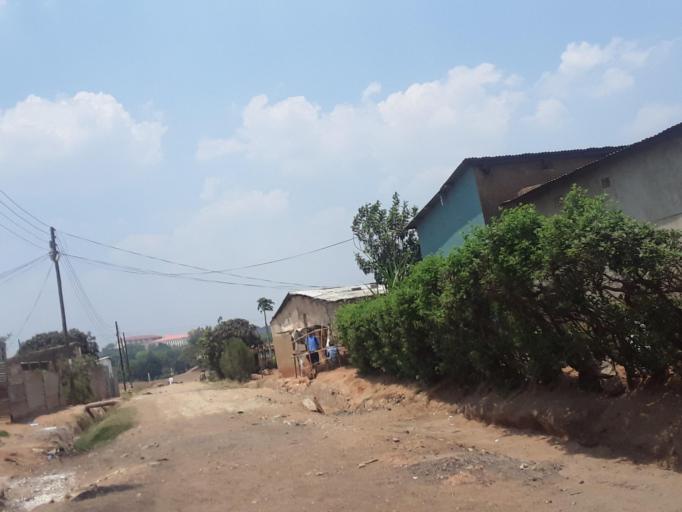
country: ZM
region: Lusaka
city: Lusaka
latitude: -15.3665
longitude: 28.2978
